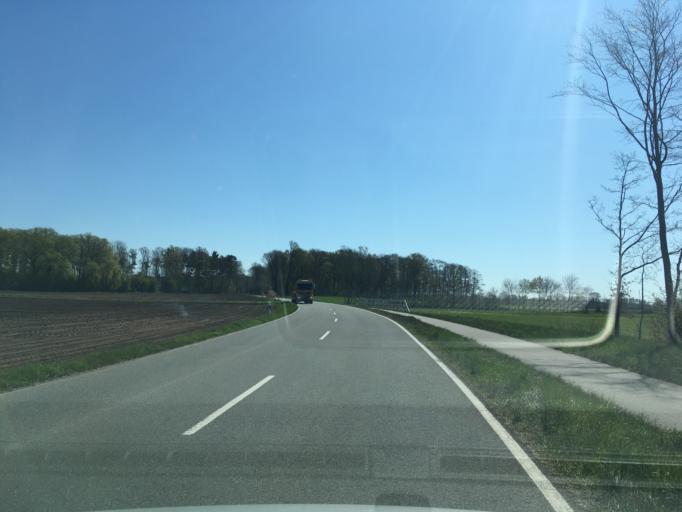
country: DE
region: North Rhine-Westphalia
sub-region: Regierungsbezirk Munster
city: Vreden
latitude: 51.9971
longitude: 6.8517
